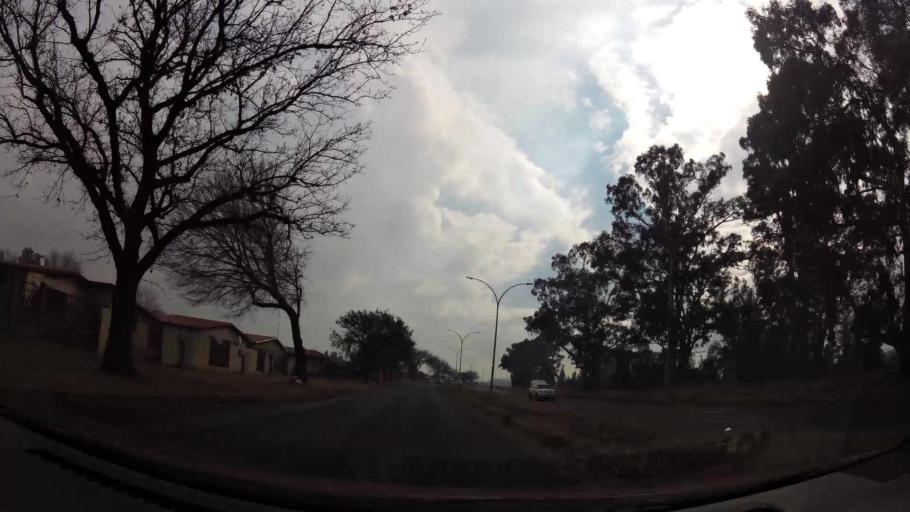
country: ZA
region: Gauteng
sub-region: Sedibeng District Municipality
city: Vanderbijlpark
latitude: -26.6771
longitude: 27.8379
